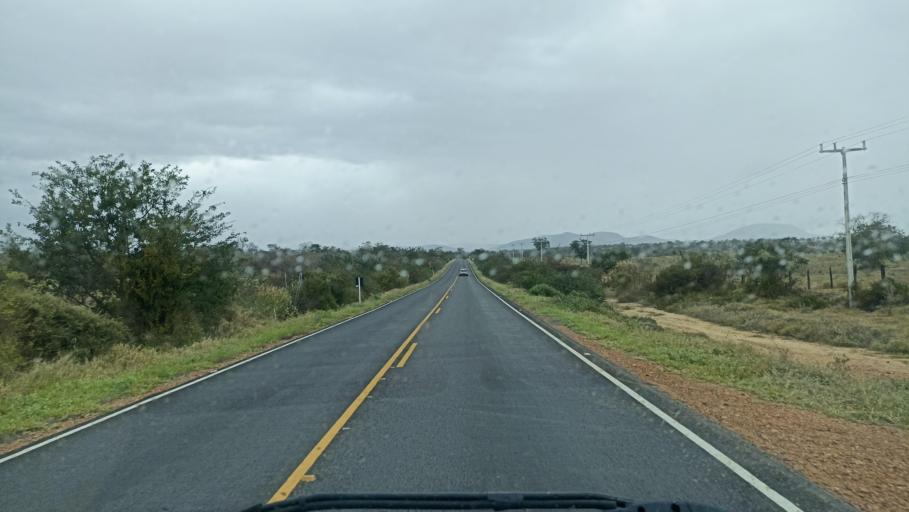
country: BR
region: Bahia
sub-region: Maracas
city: Maracas
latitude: -13.0414
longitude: -40.7032
